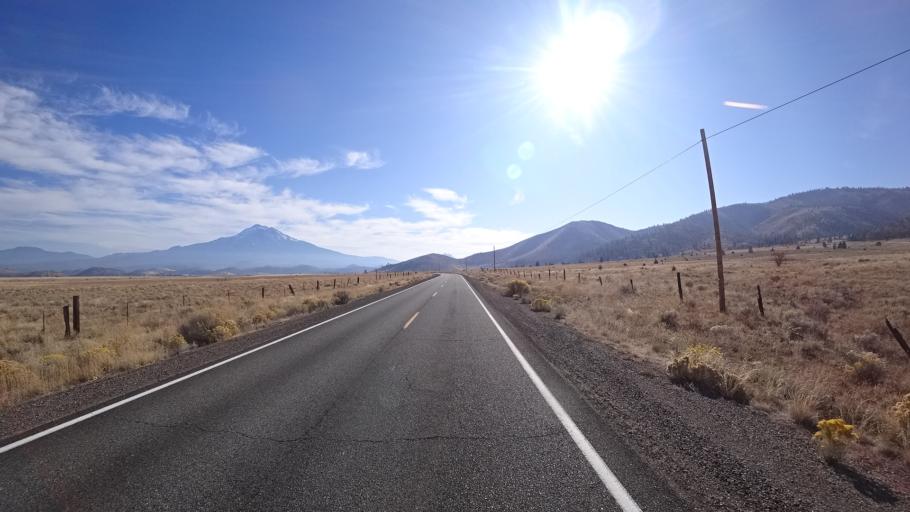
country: US
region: California
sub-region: Siskiyou County
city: Weed
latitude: 41.4799
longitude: -122.4944
